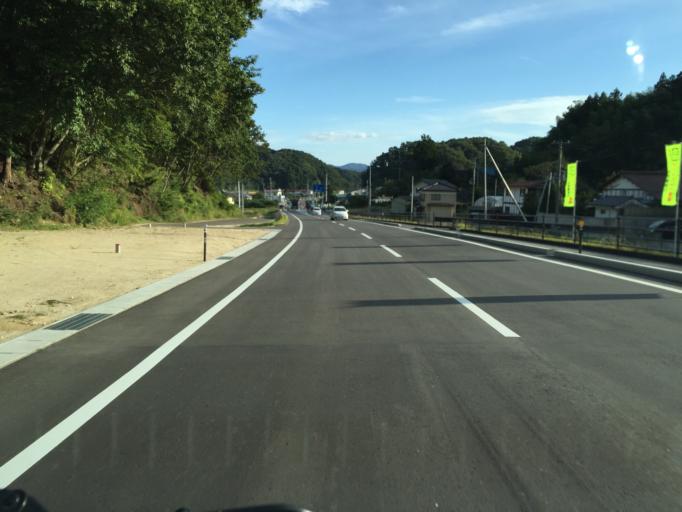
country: JP
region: Fukushima
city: Hobaramachi
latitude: 37.7332
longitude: 140.6035
